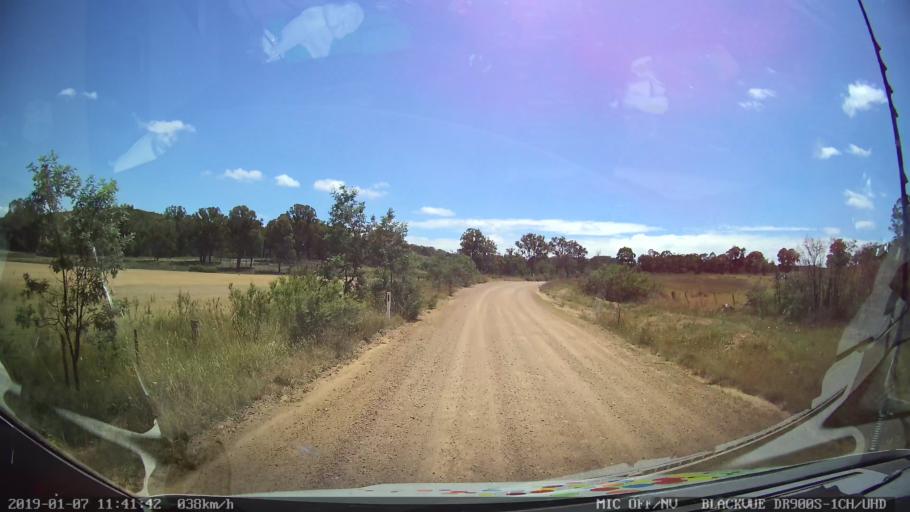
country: AU
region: New South Wales
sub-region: Guyra
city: Guyra
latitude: -30.3592
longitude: 151.5896
